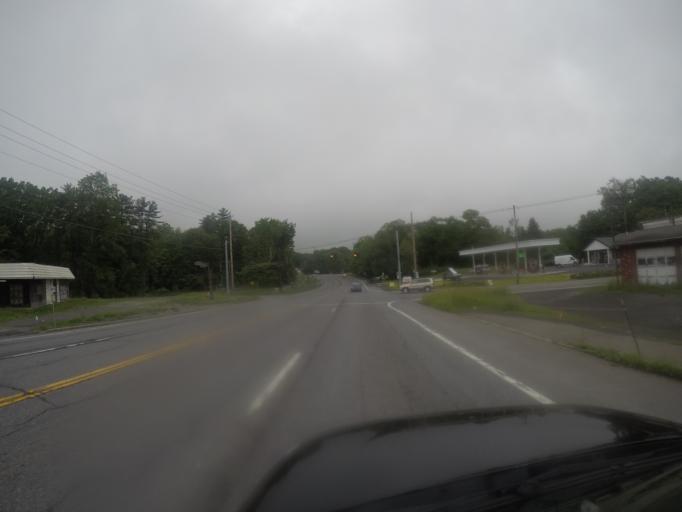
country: US
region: New York
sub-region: Ulster County
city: West Hurley
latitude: 41.9933
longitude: -74.0873
